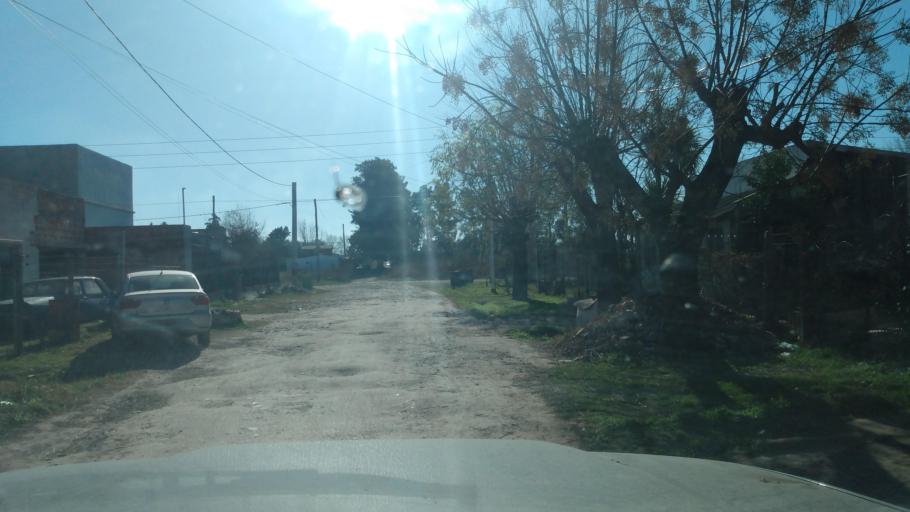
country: AR
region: Buenos Aires
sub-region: Partido de Lujan
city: Lujan
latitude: -34.5672
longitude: -59.0901
